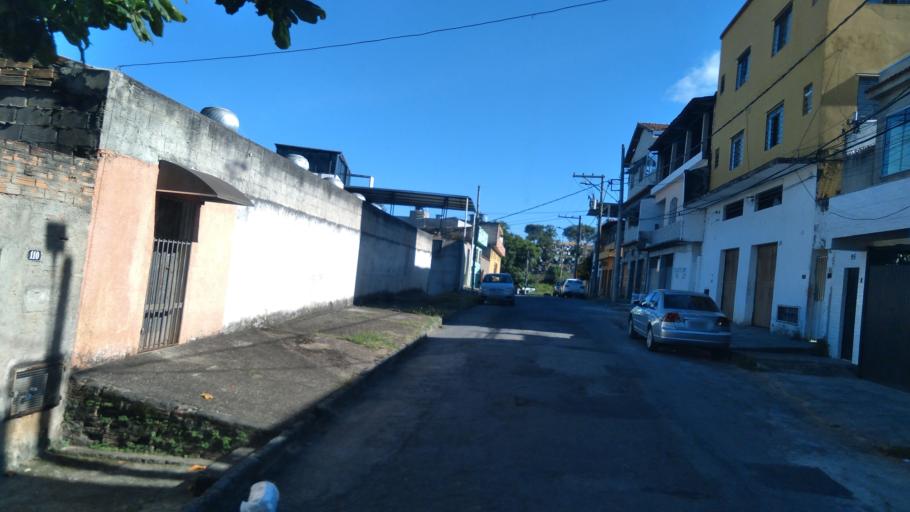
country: BR
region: Minas Gerais
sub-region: Belo Horizonte
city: Belo Horizonte
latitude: -19.9206
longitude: -43.8968
